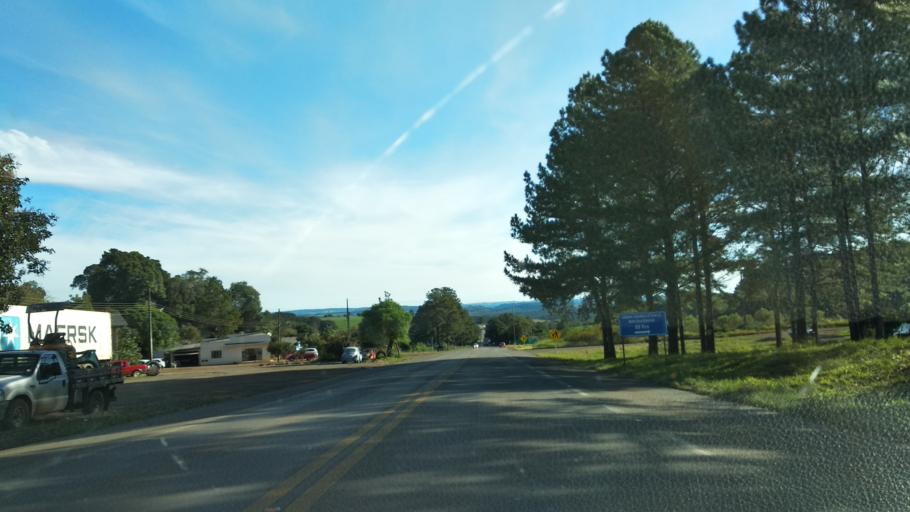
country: BR
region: Santa Catarina
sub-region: Celso Ramos
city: Celso Ramos
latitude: -27.5294
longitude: -51.3858
